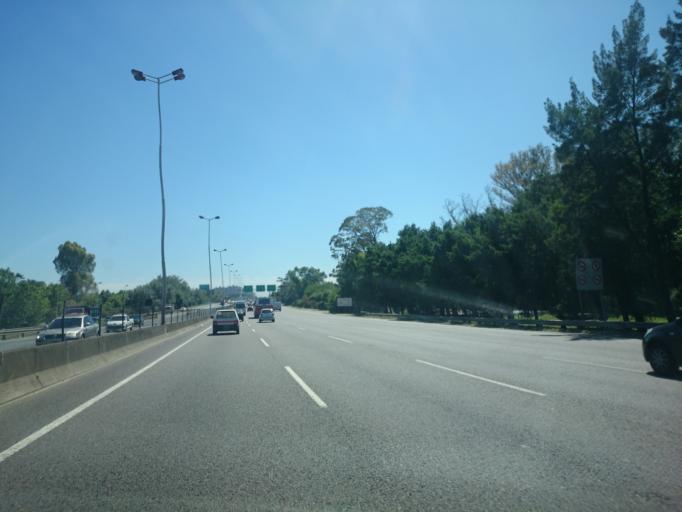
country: AR
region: Buenos Aires F.D.
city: Villa Lugano
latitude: -34.7195
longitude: -58.5116
